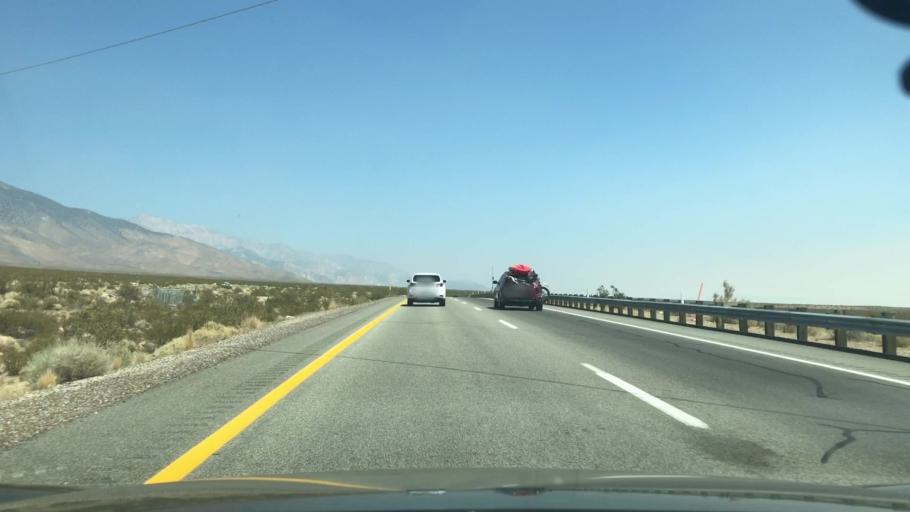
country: US
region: California
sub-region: Kern County
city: Inyokern
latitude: 36.1082
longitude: -117.9693
